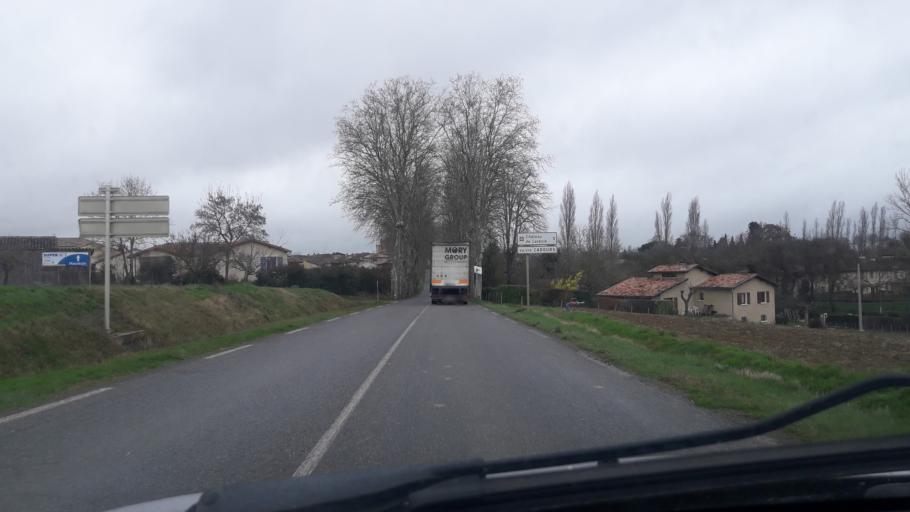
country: FR
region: Midi-Pyrenees
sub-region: Departement du Gers
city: Gimont
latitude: 43.7179
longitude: 0.9822
